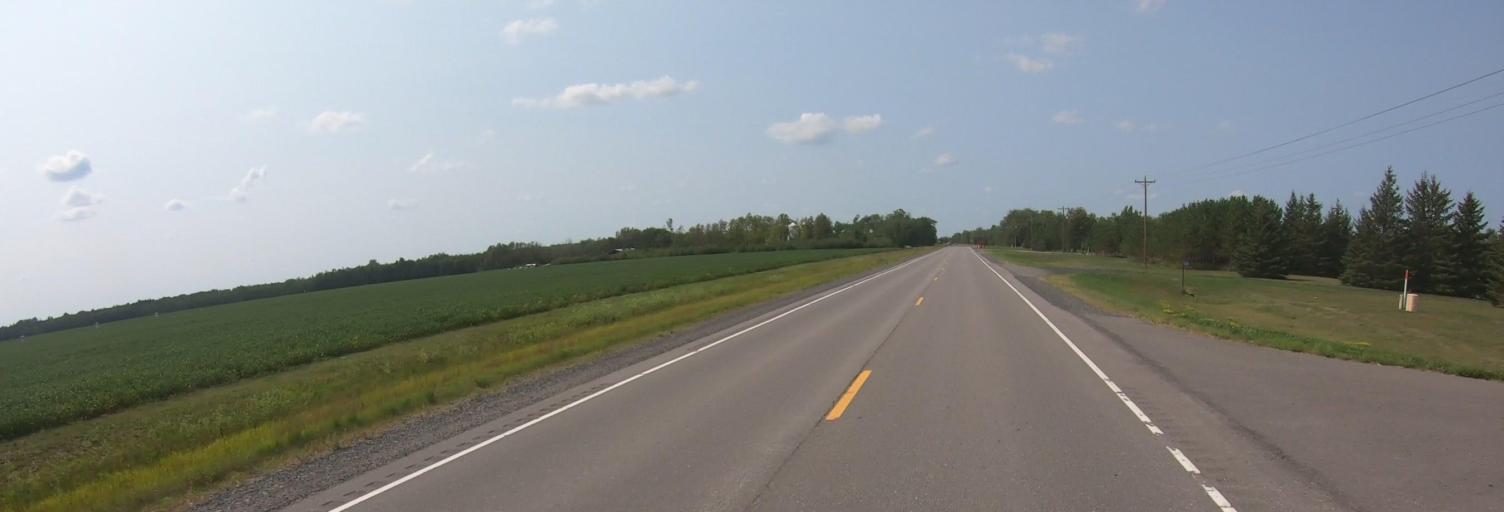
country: US
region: Minnesota
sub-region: Lake of the Woods County
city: Baudette
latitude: 48.6928
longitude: -94.4652
